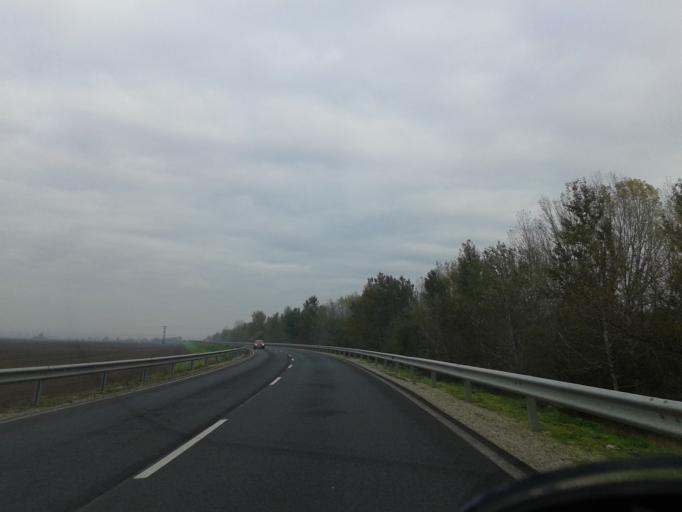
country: HU
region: Fejer
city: Ercsi
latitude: 47.2084
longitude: 18.8831
